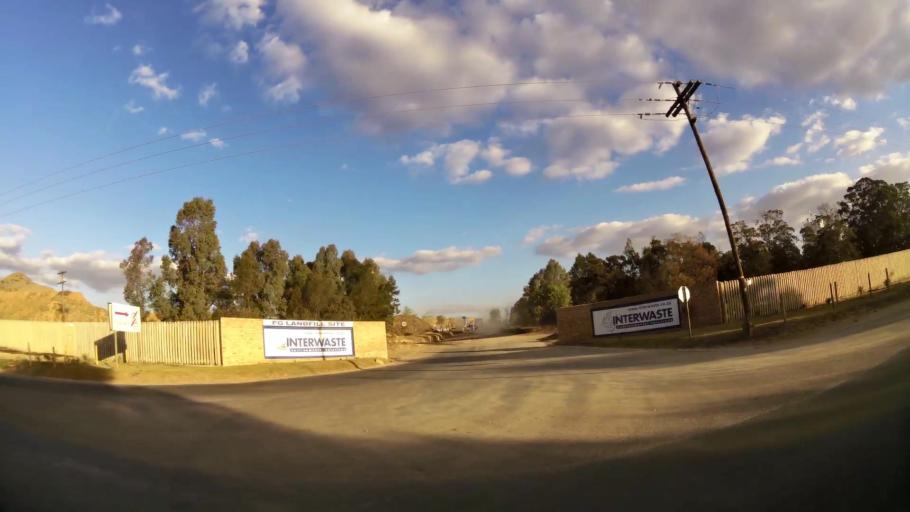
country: ZA
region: Gauteng
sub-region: Ekurhuleni Metropolitan Municipality
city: Tembisa
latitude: -25.9555
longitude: 28.1812
